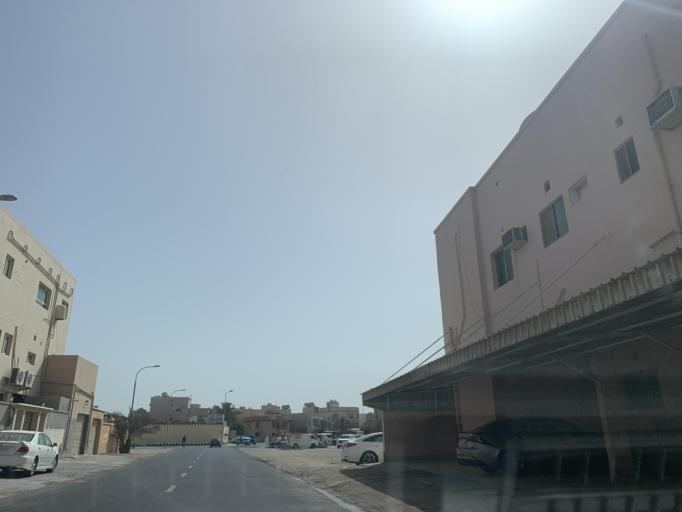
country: BH
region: Northern
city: Ar Rifa'
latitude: 26.1519
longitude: 50.5797
